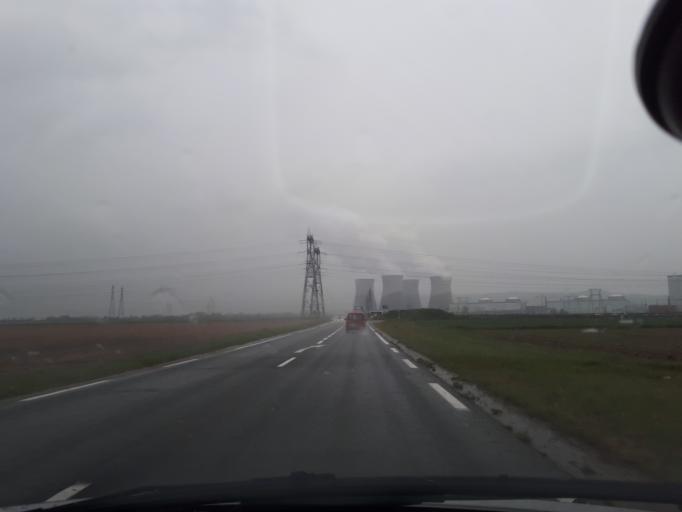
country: FR
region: Rhone-Alpes
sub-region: Departement de l'Isere
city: Hieres-sur-Amby
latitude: 45.7950
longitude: 5.2508
